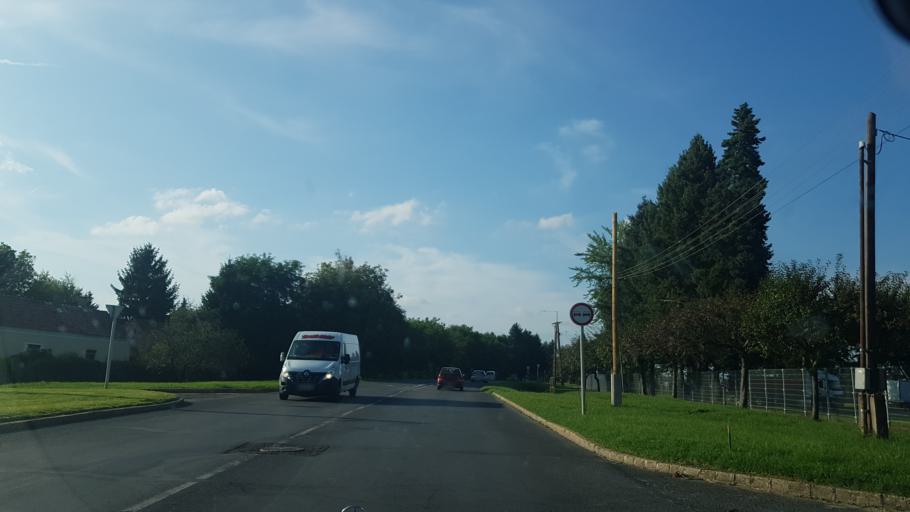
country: HU
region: Somogy
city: Nagyatad
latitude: 46.2395
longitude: 17.3561
